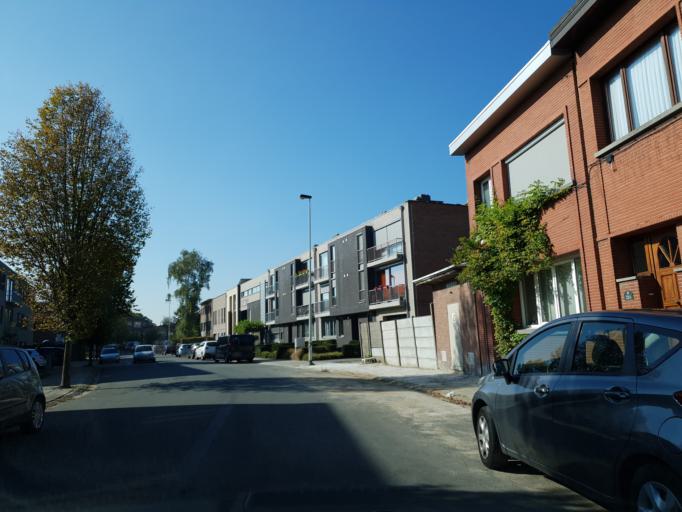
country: BE
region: Flanders
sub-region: Provincie Antwerpen
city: Borsbeek
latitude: 51.2022
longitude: 4.4780
